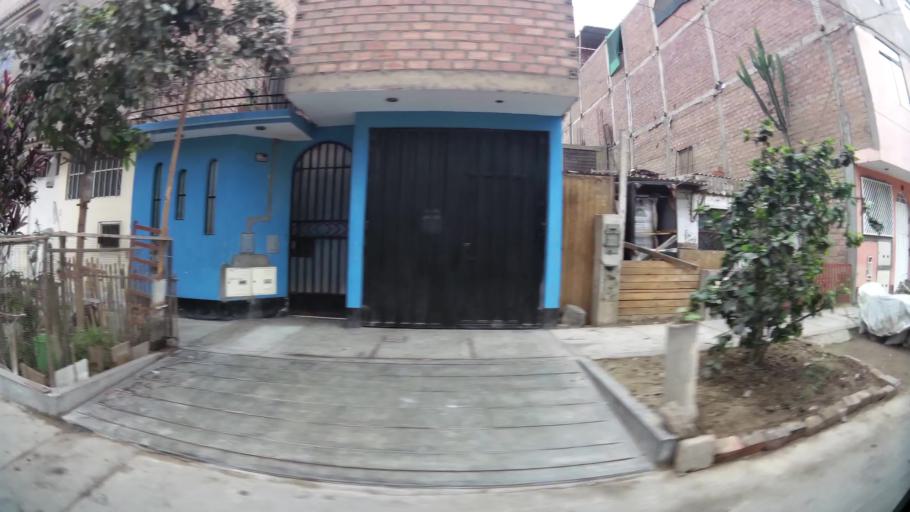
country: PE
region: Lima
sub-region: Lima
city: Independencia
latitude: -11.9652
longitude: -77.0775
